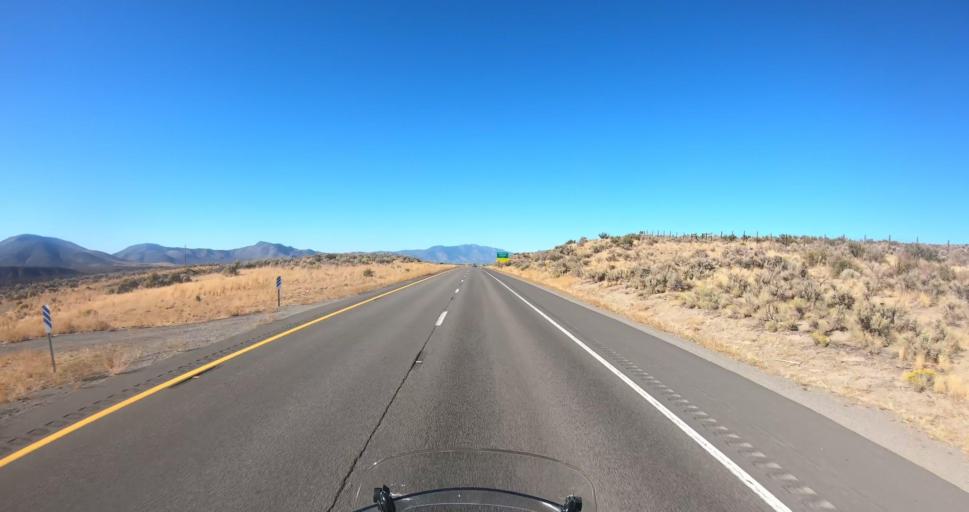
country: US
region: Nevada
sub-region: Washoe County
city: Cold Springs
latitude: 39.7109
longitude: -120.0352
